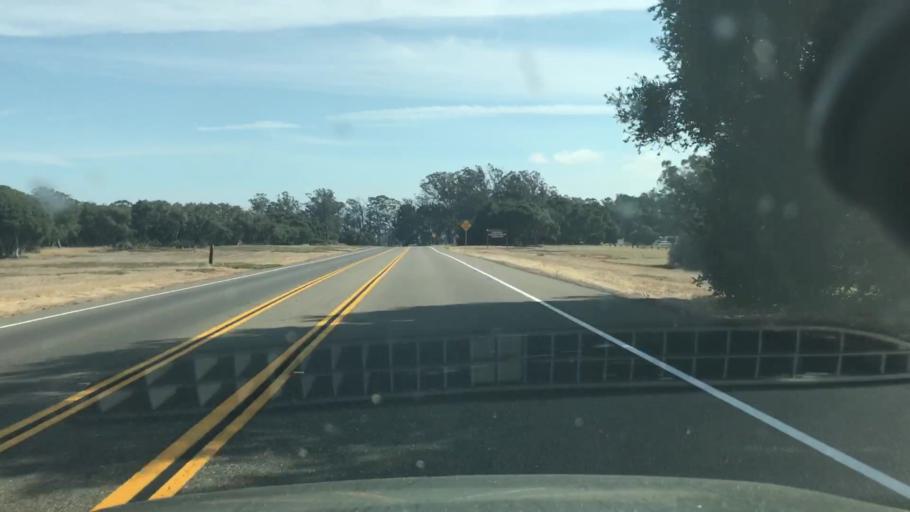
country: US
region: California
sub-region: Santa Barbara County
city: Vandenberg Village
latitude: 34.6877
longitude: -120.5020
